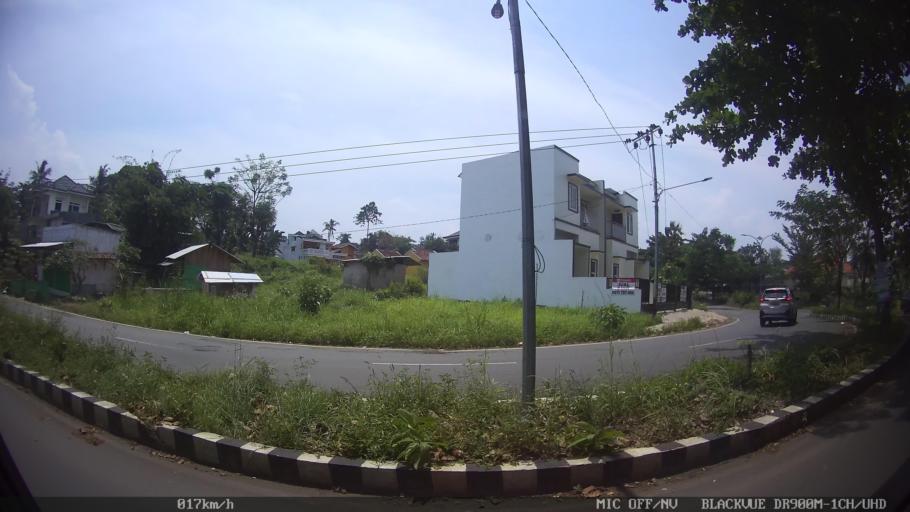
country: ID
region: Lampung
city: Bandarlampung
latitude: -5.4373
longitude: 105.2483
